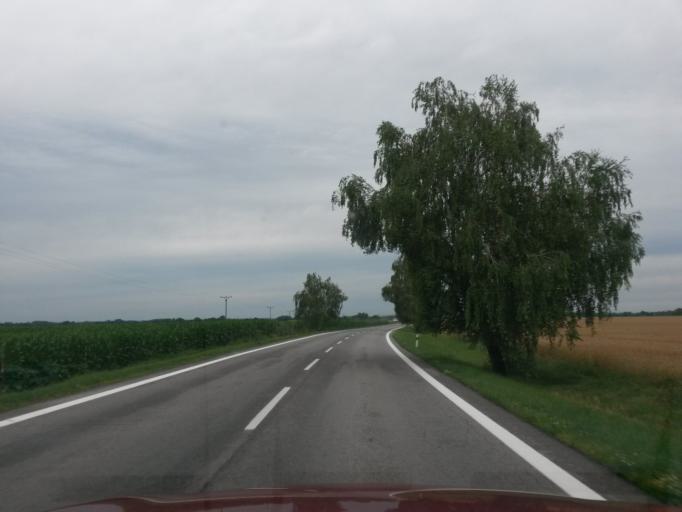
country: SK
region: Nitriansky
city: Zeliezovce
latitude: 48.1241
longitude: 18.6914
